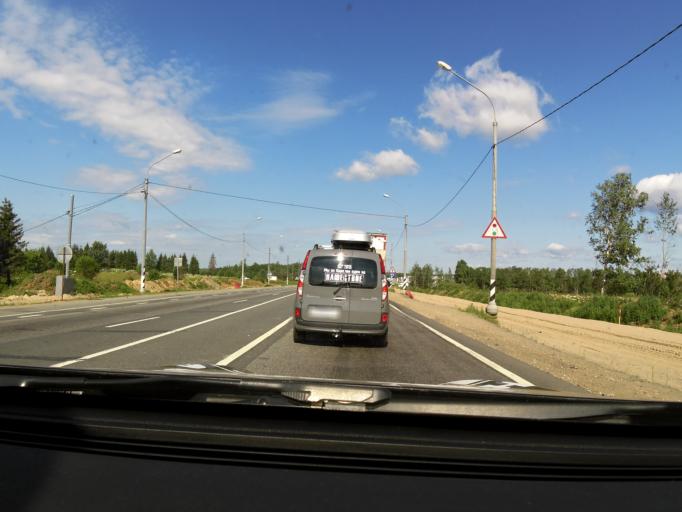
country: RU
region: Tverskaya
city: Tver
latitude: 56.7877
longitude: 35.9186
